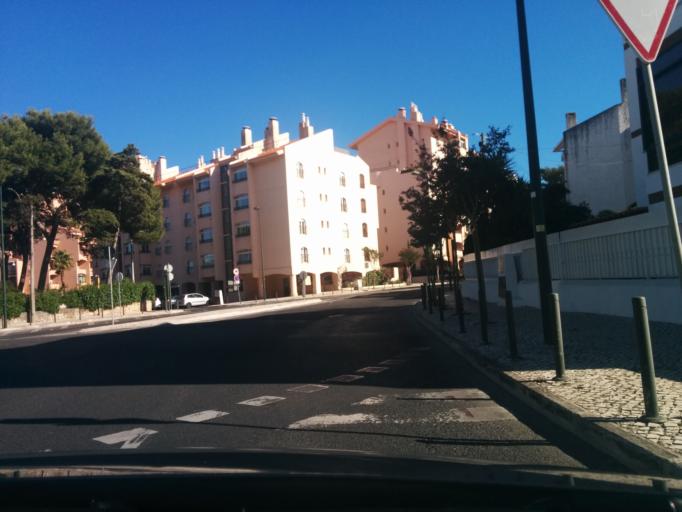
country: PT
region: Lisbon
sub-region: Cascais
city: Cascais
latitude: 38.6961
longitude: -9.4304
